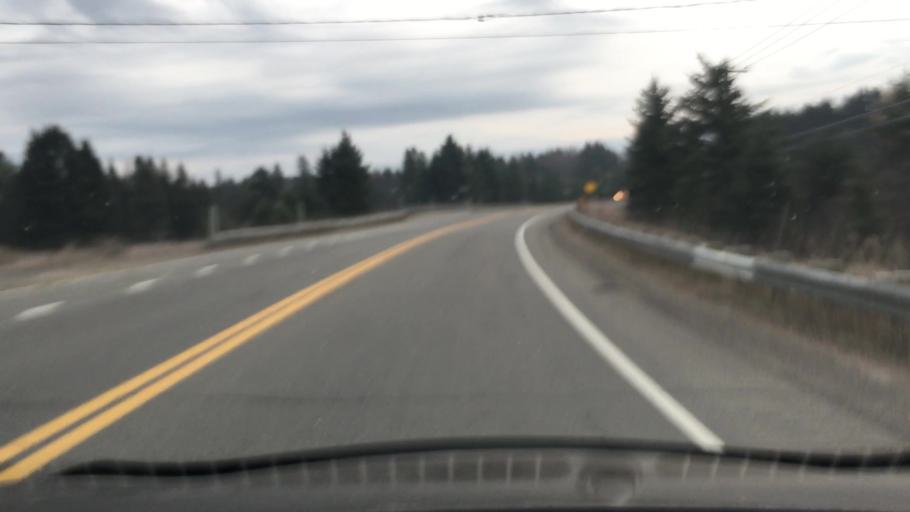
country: CA
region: Quebec
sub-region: Laurentides
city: Saint-Sauveur
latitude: 45.9035
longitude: -74.2364
